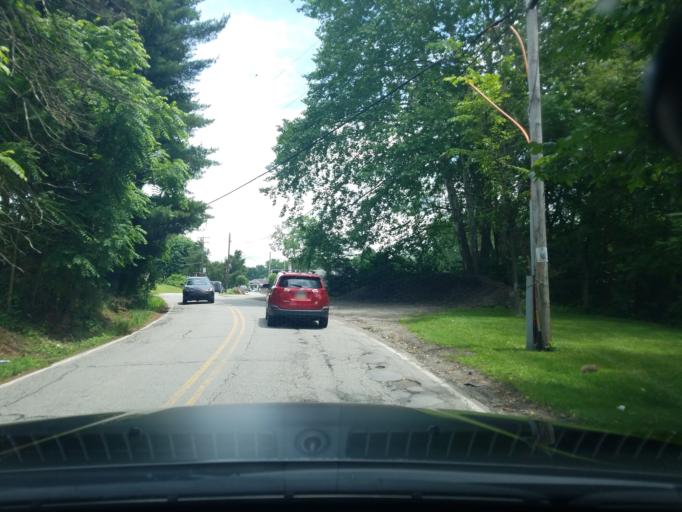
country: US
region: Pennsylvania
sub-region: Westmoreland County
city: Youngwood
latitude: 40.2283
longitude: -79.5880
